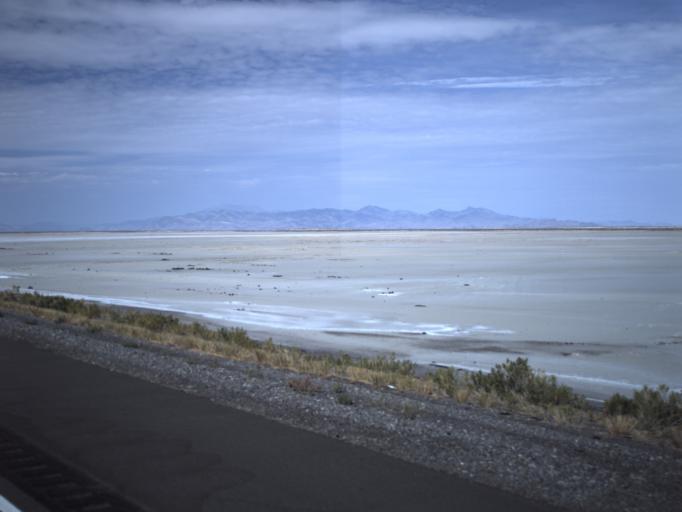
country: US
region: Utah
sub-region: Tooele County
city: Wendover
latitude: 40.7306
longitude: -113.4486
